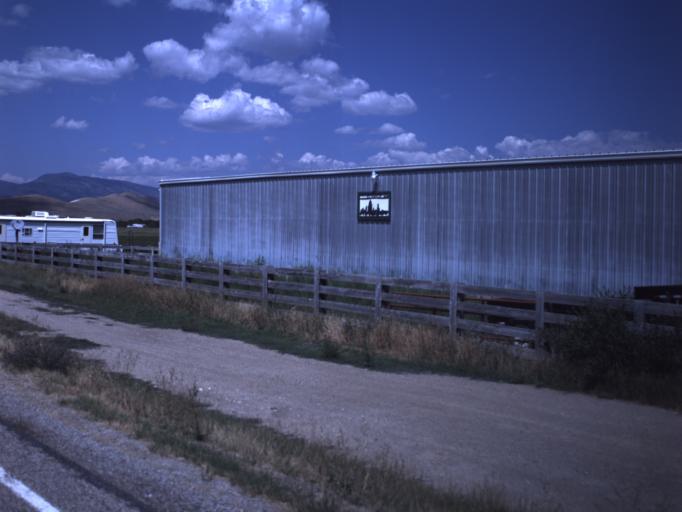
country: US
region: Utah
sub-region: Rich County
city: Randolph
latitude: 41.8400
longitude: -111.3422
